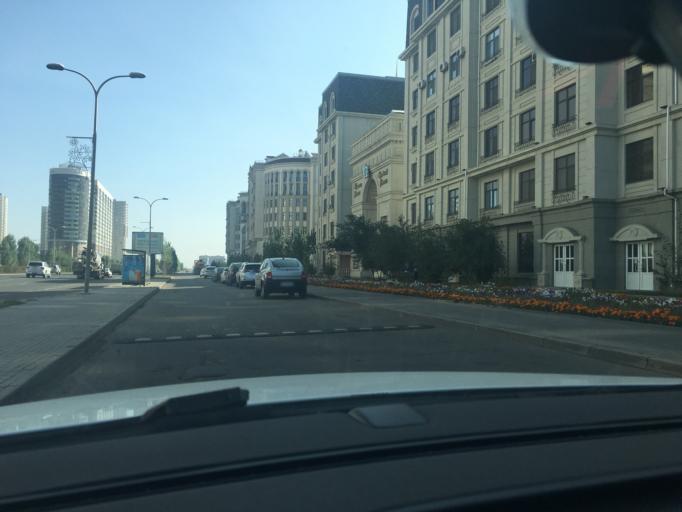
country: KZ
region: Astana Qalasy
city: Astana
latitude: 51.1190
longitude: 71.4544
